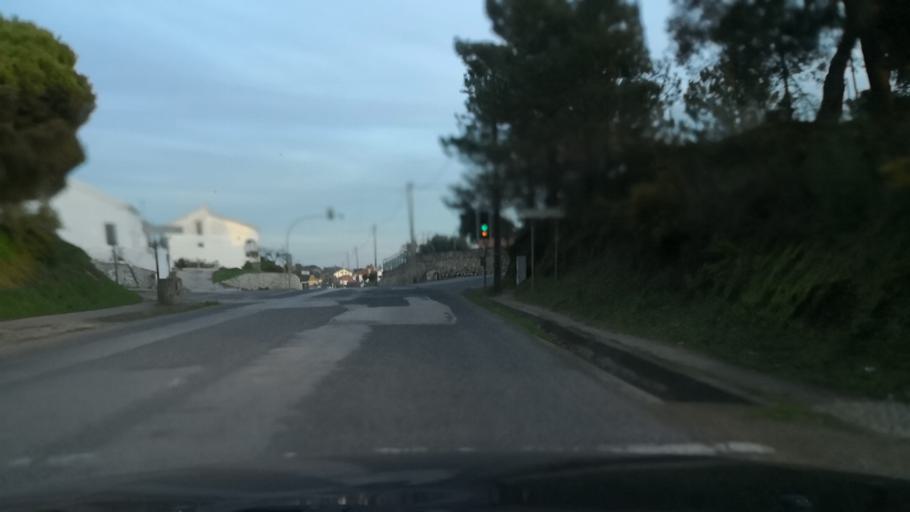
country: PT
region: Setubal
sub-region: Setubal
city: Setubal
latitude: 38.5236
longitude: -8.8390
